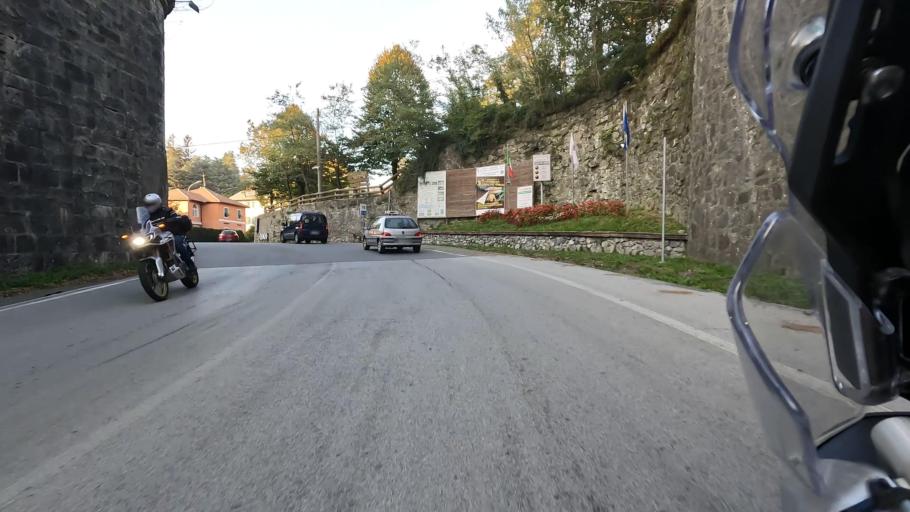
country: IT
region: Liguria
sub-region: Provincia di Savona
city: Osteria dei Cacciatori-Stella
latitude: 44.4286
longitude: 8.4737
